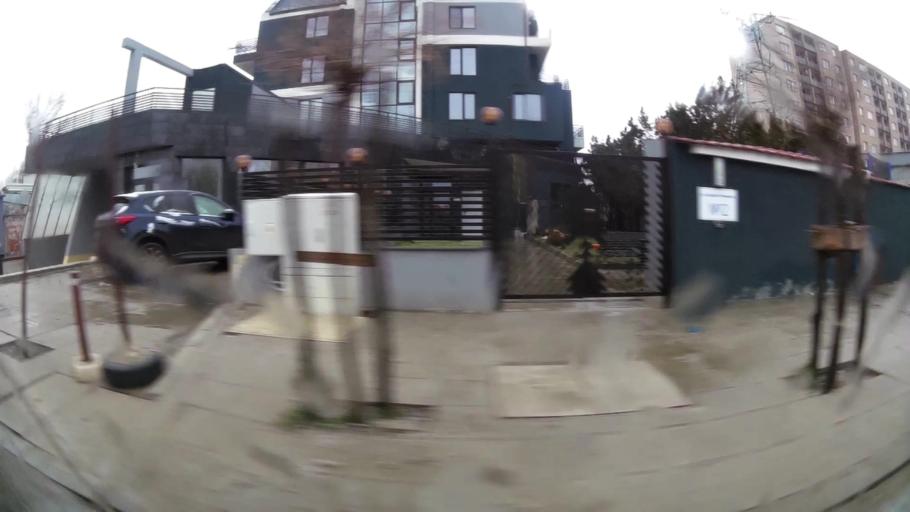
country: BG
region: Sofia-Capital
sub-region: Stolichna Obshtina
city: Sofia
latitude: 42.6546
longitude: 23.3172
